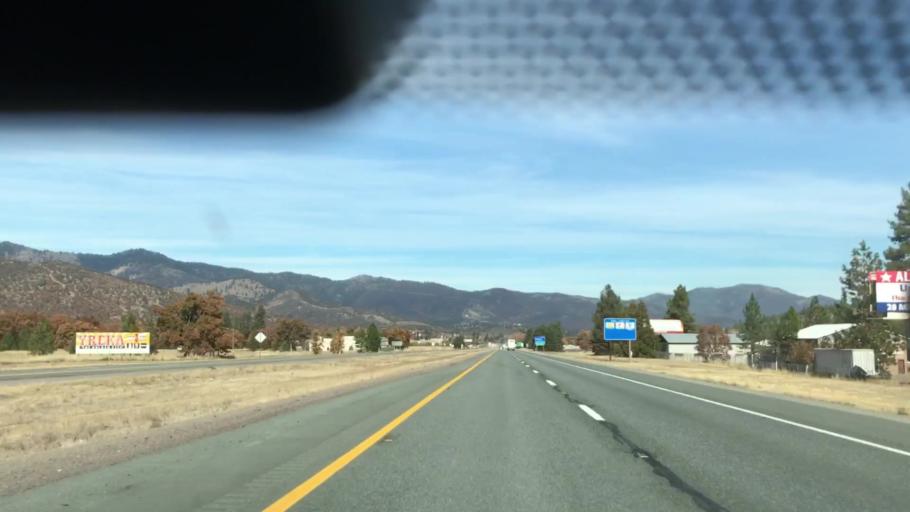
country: US
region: California
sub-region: Siskiyou County
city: Yreka
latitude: 41.6891
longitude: -122.6373
